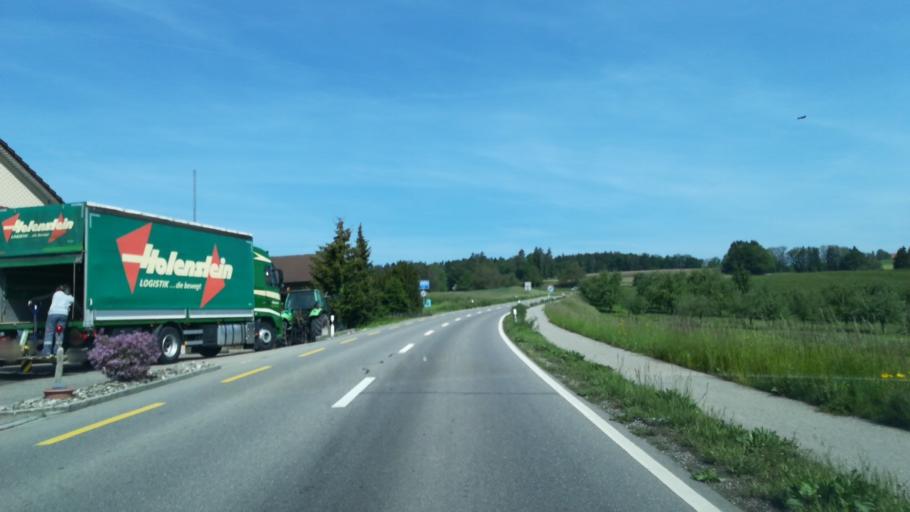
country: CH
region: Thurgau
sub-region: Frauenfeld District
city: Pfyn
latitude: 47.6017
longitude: 8.9476
